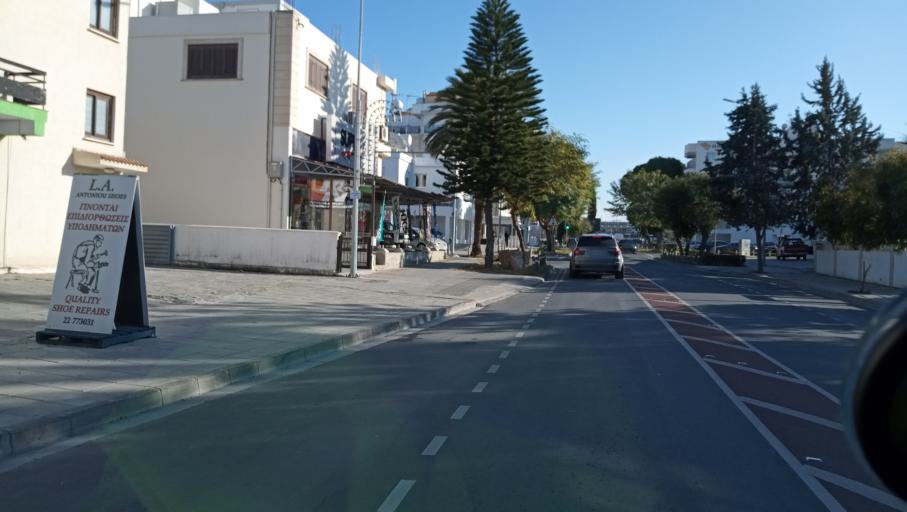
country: CY
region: Lefkosia
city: Nicosia
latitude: 35.1713
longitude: 33.3246
